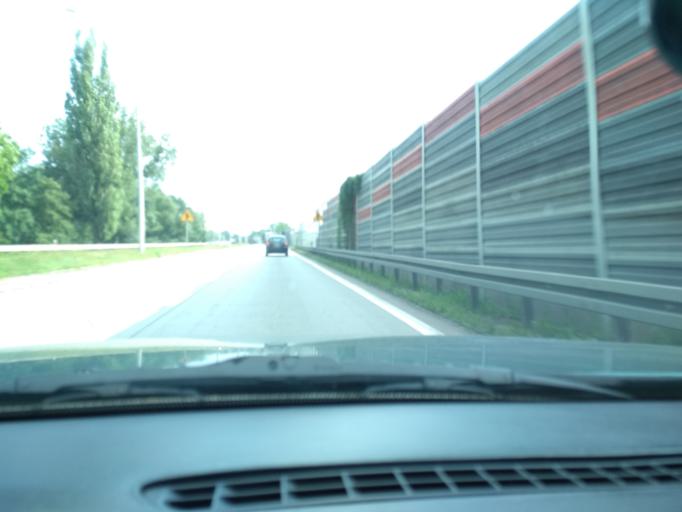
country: PL
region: Silesian Voivodeship
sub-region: Zory
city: Zory
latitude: 50.0187
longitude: 18.7076
